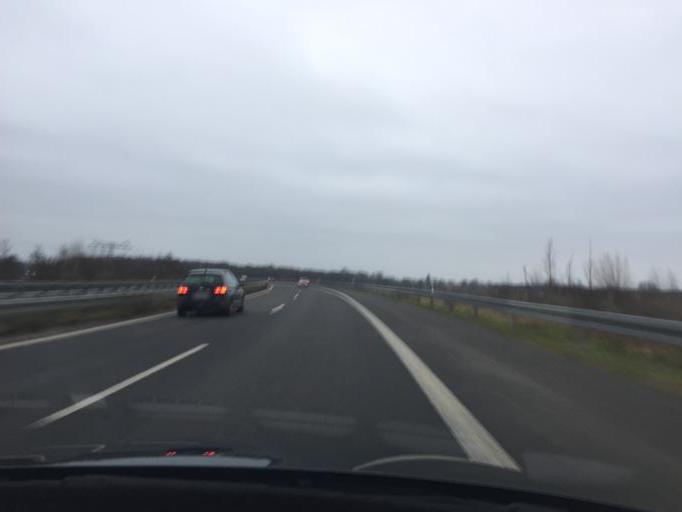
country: DE
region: Brandenburg
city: Rangsdorf
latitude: 52.3312
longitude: 13.4447
